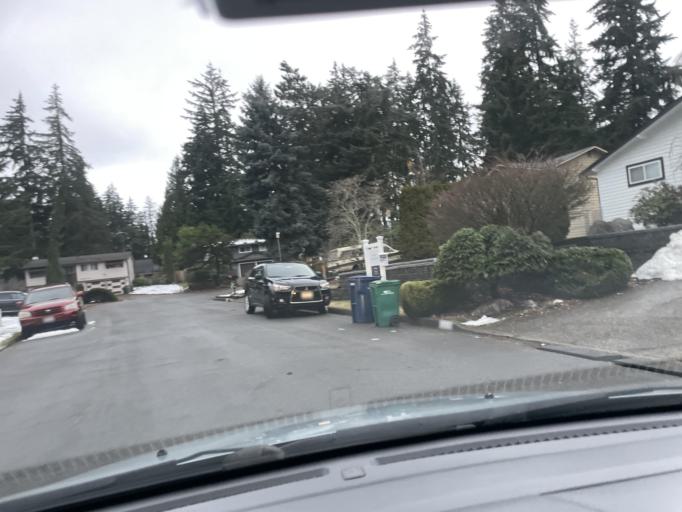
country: US
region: Washington
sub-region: King County
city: Kingsgate
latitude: 47.7244
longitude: -122.1798
